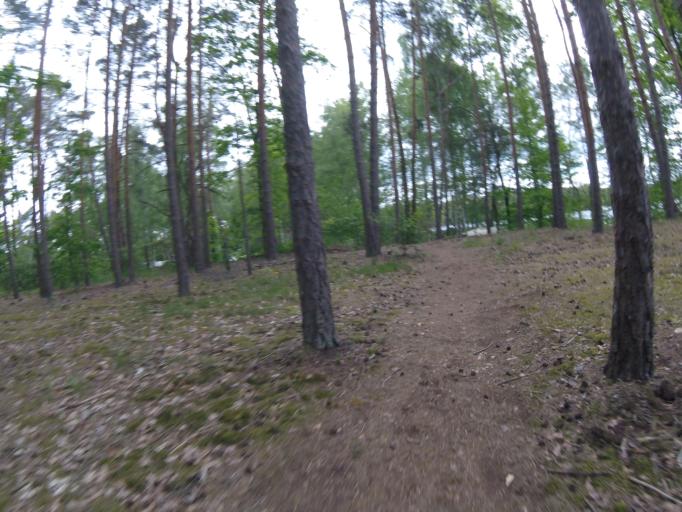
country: DE
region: Brandenburg
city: Bestensee
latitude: 52.2557
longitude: 13.6662
